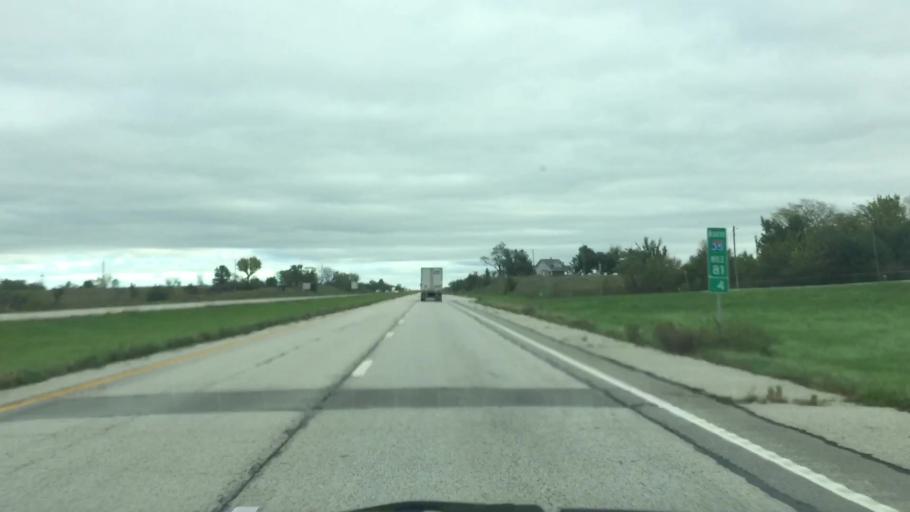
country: US
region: Missouri
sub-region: Harrison County
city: Bethany
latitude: 40.1174
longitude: -94.0607
